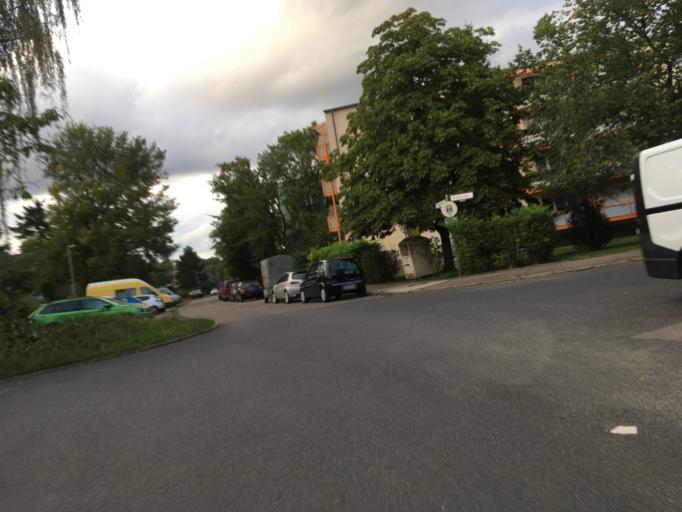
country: DE
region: Berlin
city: Johannisthal
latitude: 52.4456
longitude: 13.5008
